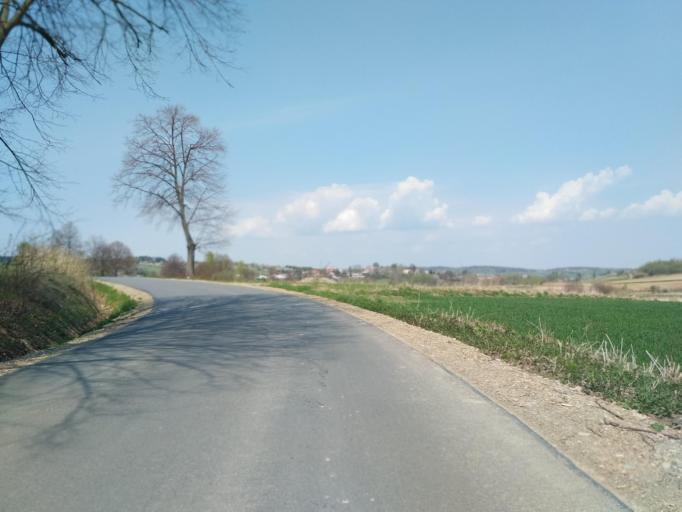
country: PL
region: Subcarpathian Voivodeship
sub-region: Powiat krosnienski
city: Chorkowka
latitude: 49.6402
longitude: 21.6814
